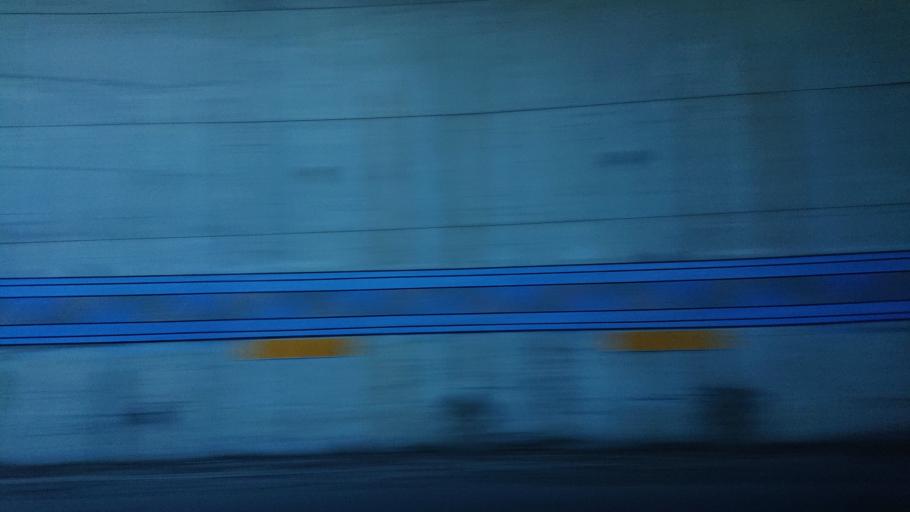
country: TW
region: Taiwan
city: Lugu
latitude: 23.4740
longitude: 120.8382
